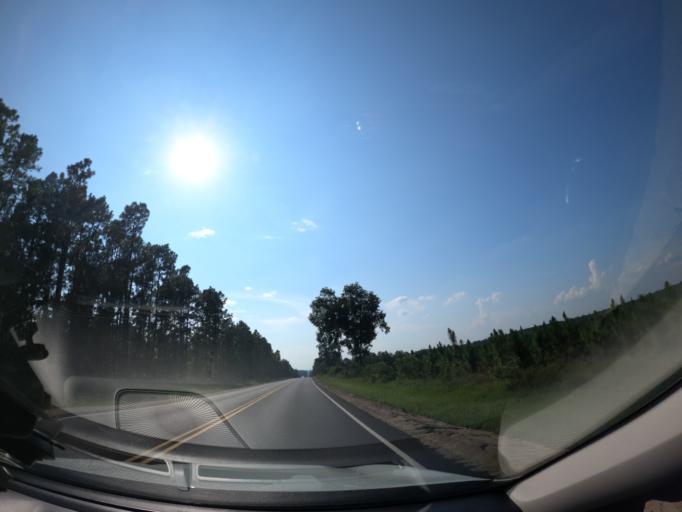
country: US
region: South Carolina
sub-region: Aiken County
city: New Ellenton
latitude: 33.3943
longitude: -81.7385
